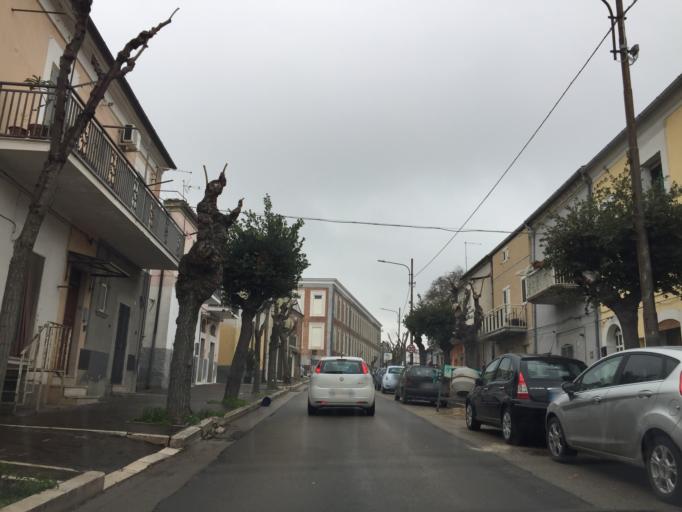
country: IT
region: Apulia
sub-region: Provincia di Foggia
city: Troia
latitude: 41.3632
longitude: 15.3110
